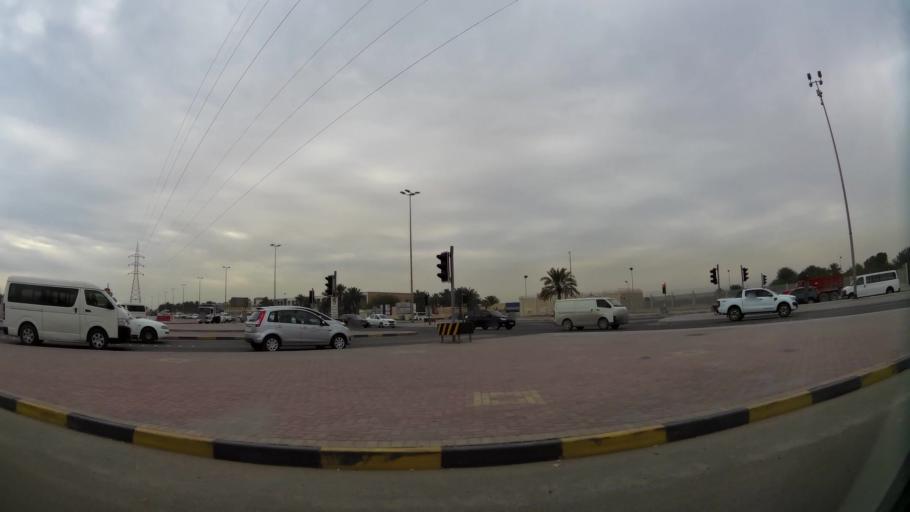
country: BH
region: Northern
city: Sitrah
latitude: 26.1650
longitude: 50.6048
